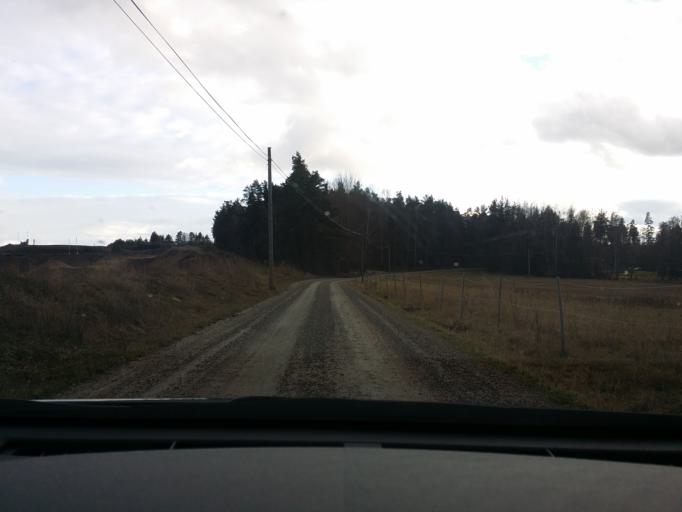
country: SE
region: Soedermanland
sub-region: Eskilstuna Kommun
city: Arla
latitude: 59.3732
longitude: 16.6740
